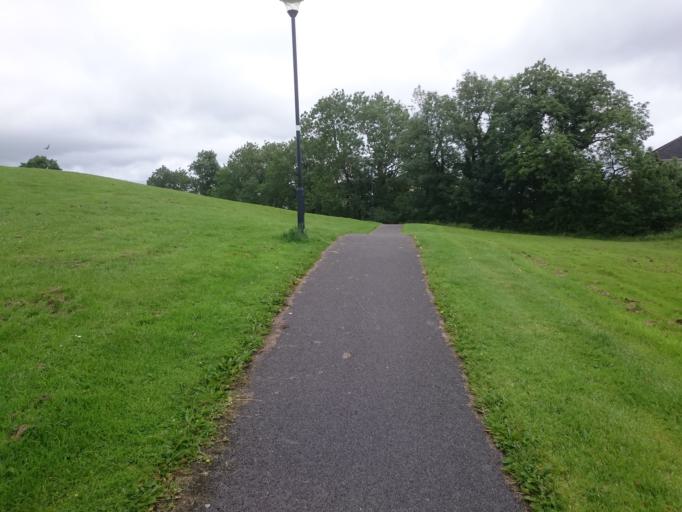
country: IE
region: Connaught
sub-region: Maigh Eo
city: Ballyhaunis
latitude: 53.7619
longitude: -8.7608
